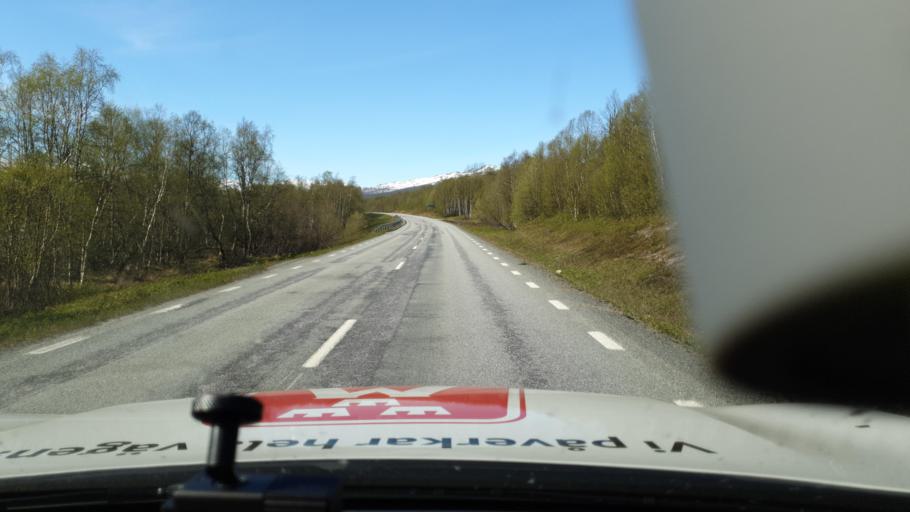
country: NO
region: Nordland
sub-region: Rana
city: Mo i Rana
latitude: 65.7895
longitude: 15.1044
